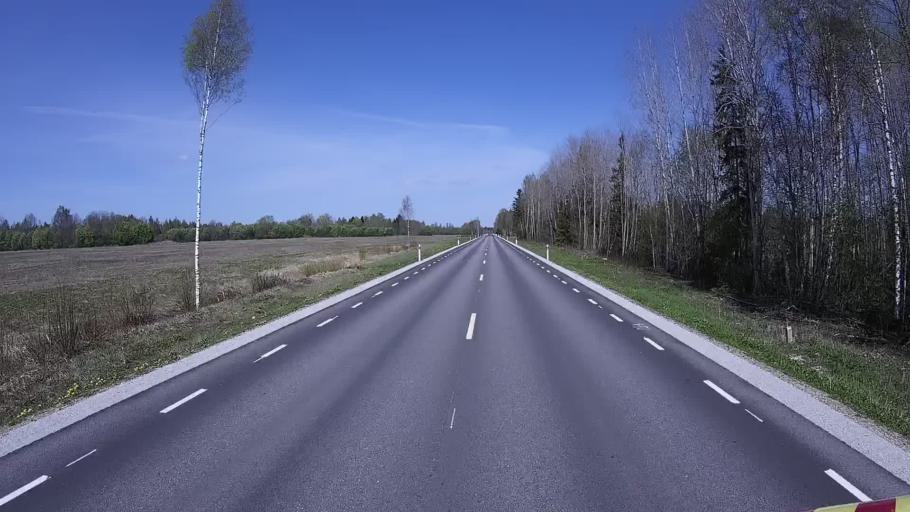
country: EE
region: Harju
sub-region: Nissi vald
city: Turba
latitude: 59.1608
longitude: 24.0740
